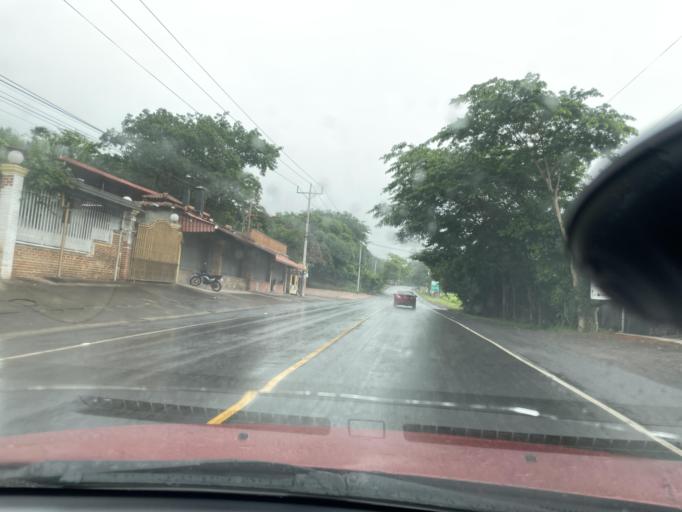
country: SV
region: Morazan
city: Jocoro
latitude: 13.5646
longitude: -88.0962
